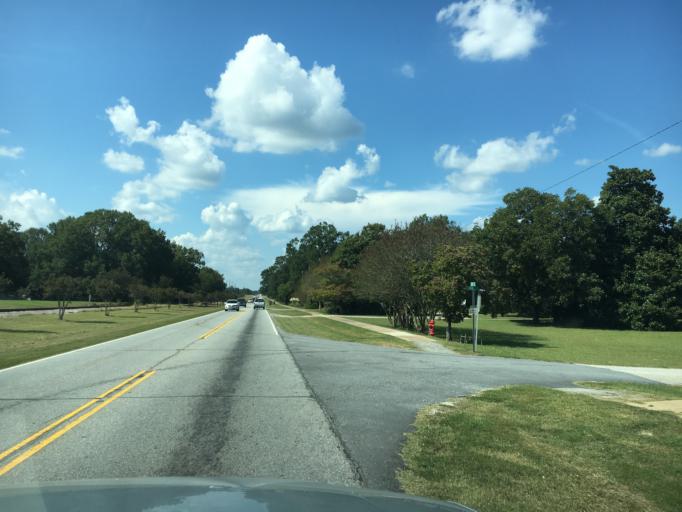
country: US
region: South Carolina
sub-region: Greenville County
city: Fountain Inn
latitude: 34.6109
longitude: -82.1162
